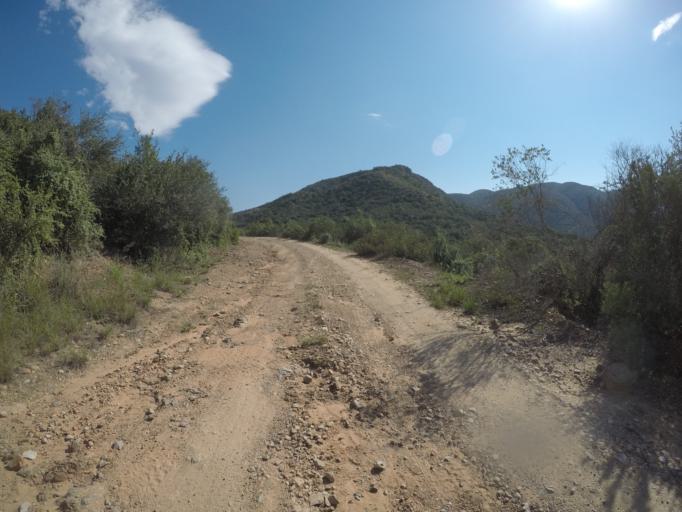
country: ZA
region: Eastern Cape
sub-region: Cacadu District Municipality
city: Kareedouw
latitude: -33.6554
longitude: 24.4079
